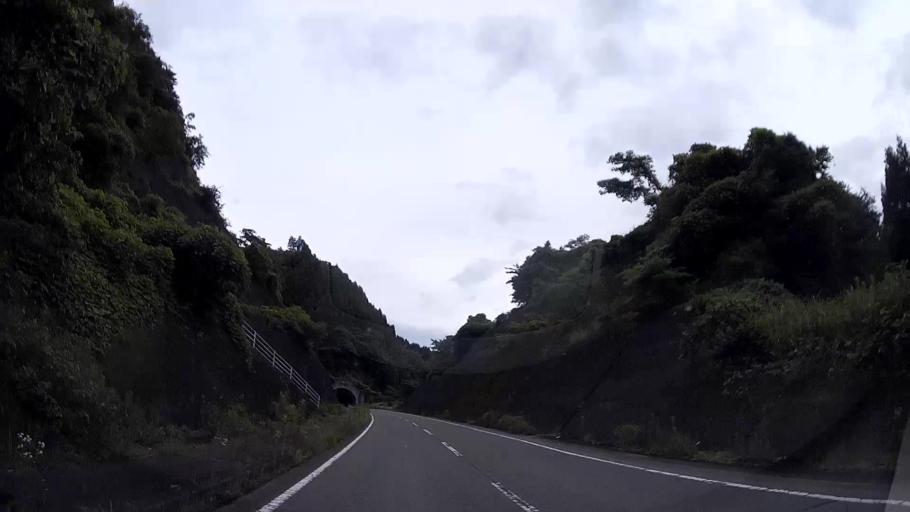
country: JP
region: Oita
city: Hita
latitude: 33.1334
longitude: 130.9883
